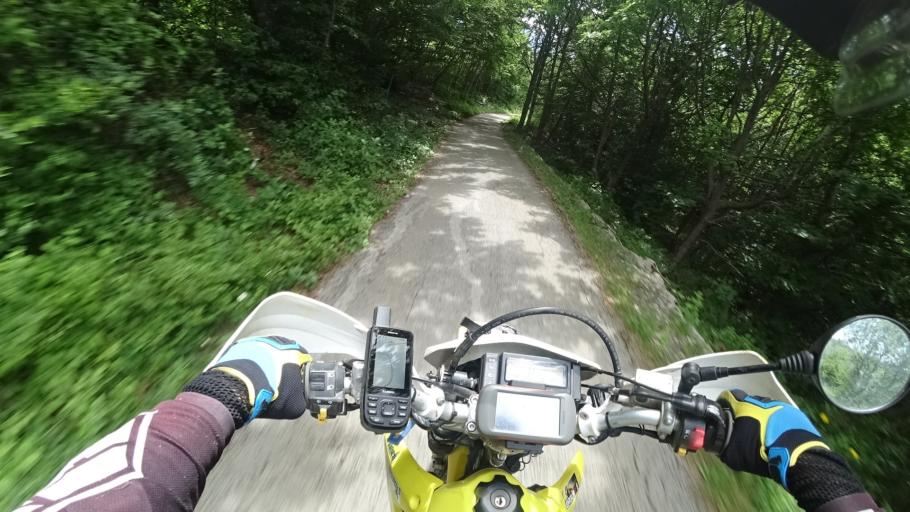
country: HR
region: Primorsko-Goranska
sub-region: Grad Crikvenica
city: Jadranovo
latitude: 45.2490
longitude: 14.6703
